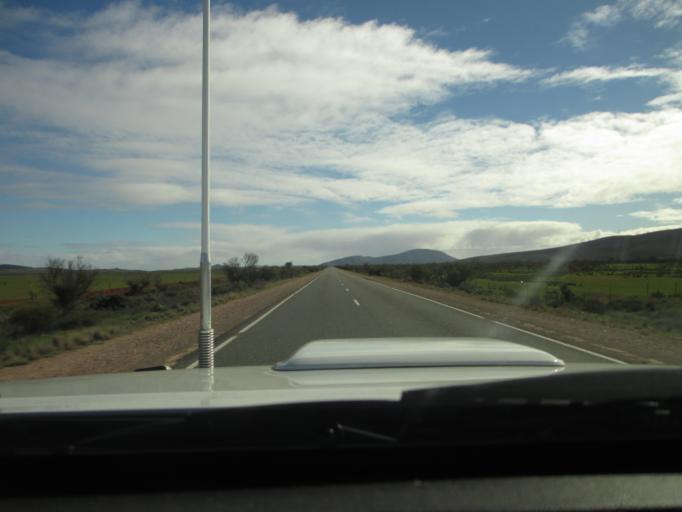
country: AU
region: South Australia
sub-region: Flinders Ranges
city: Quorn
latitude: -31.8589
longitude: 138.4015
